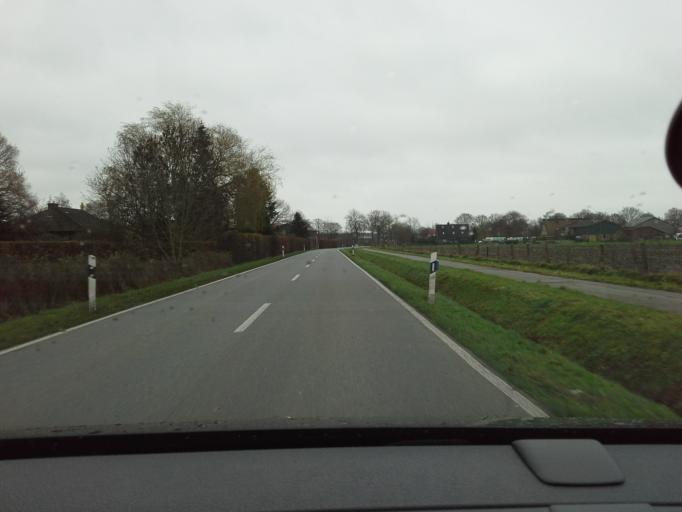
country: DE
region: Schleswig-Holstein
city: Hemdingen
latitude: 53.7650
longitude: 9.8497
